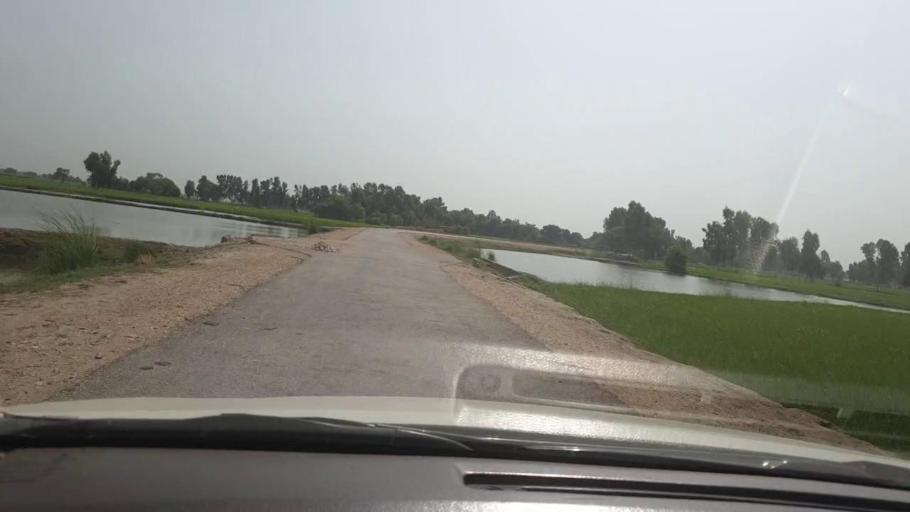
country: PK
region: Sindh
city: Rustam jo Goth
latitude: 27.9737
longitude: 68.7743
